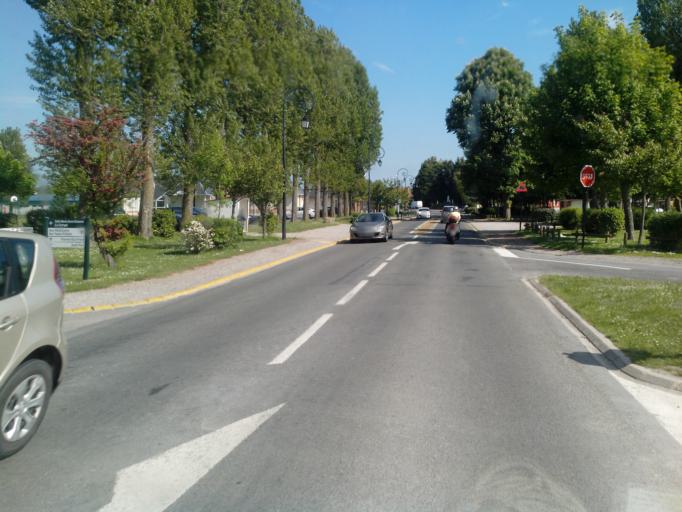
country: FR
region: Nord-Pas-de-Calais
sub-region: Departement du Pas-de-Calais
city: Groffliers
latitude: 50.3847
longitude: 1.6153
